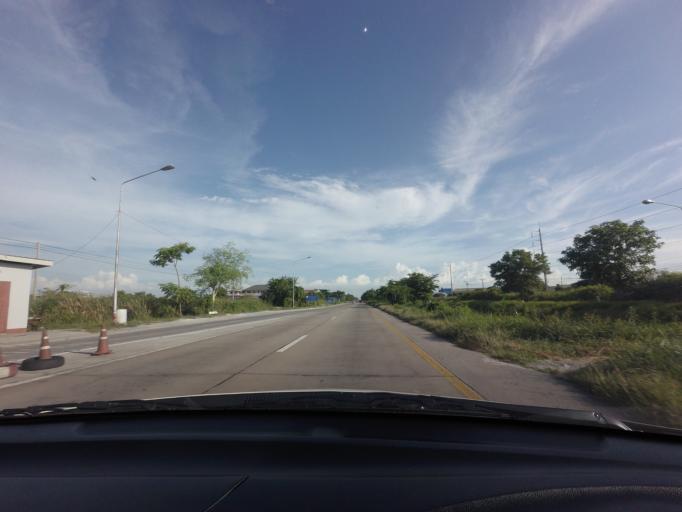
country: TH
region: Phra Nakhon Si Ayutthaya
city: Lat Bua Luang
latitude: 14.1385
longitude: 100.2901
